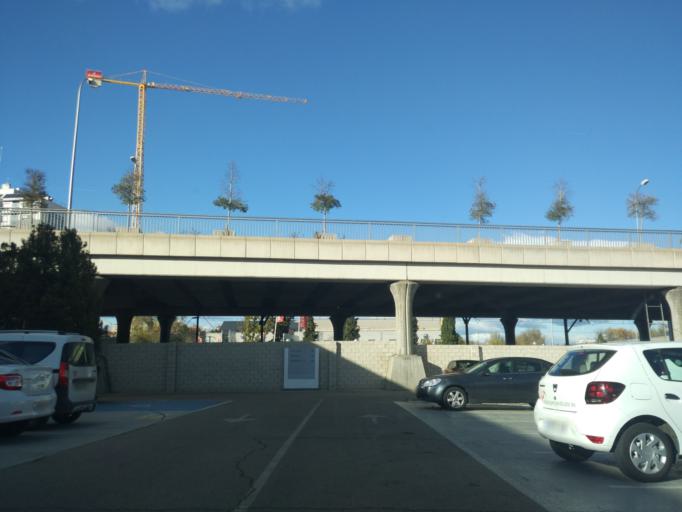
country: ES
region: Madrid
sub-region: Provincia de Madrid
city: Villaverde
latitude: 40.3453
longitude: -3.6938
